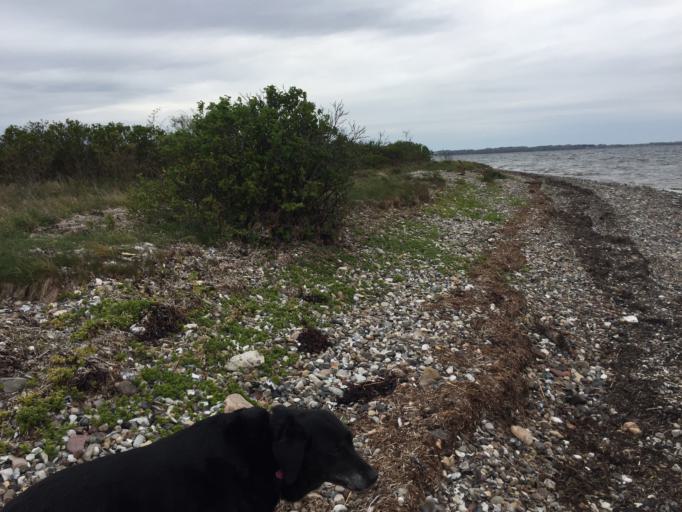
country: DK
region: South Denmark
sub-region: Assens Kommune
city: Harby
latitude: 55.1323
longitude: 10.0438
